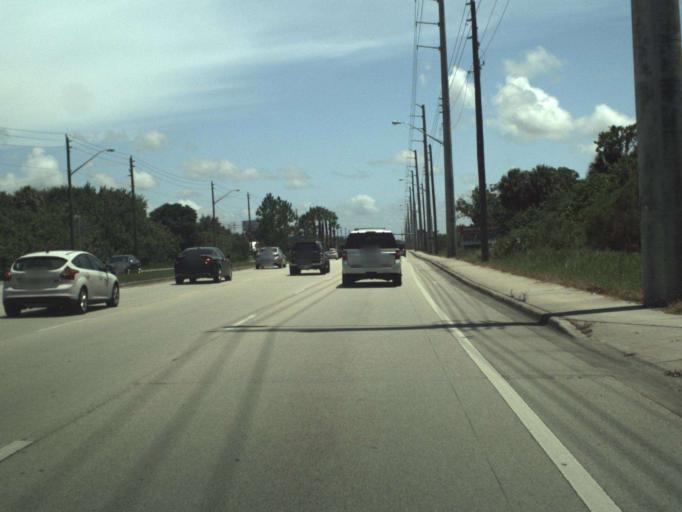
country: US
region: Florida
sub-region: Saint Lucie County
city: Indian River Estates
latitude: 27.3485
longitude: -80.3260
